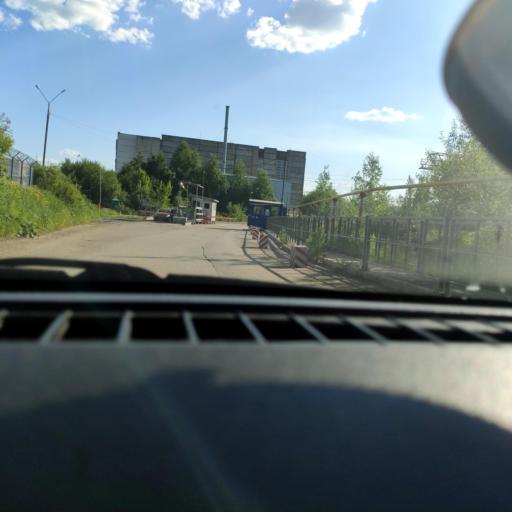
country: RU
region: Perm
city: Perm
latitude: 58.0813
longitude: 56.3458
